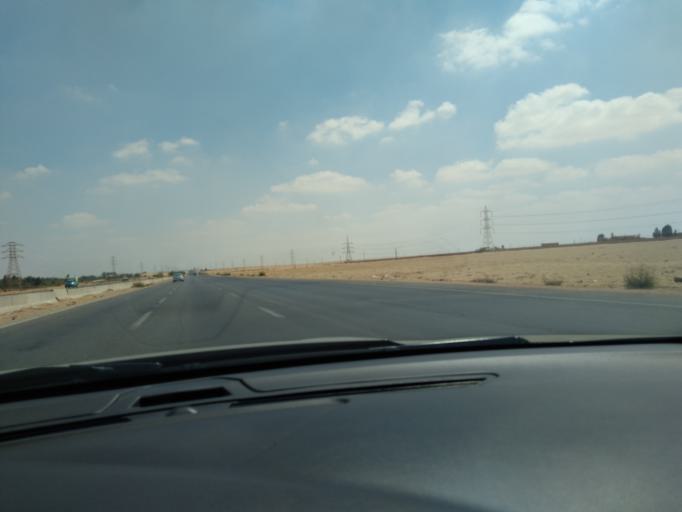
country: EG
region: Al Isma'iliyah
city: At Tall al Kabir
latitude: 30.3592
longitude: 31.9023
